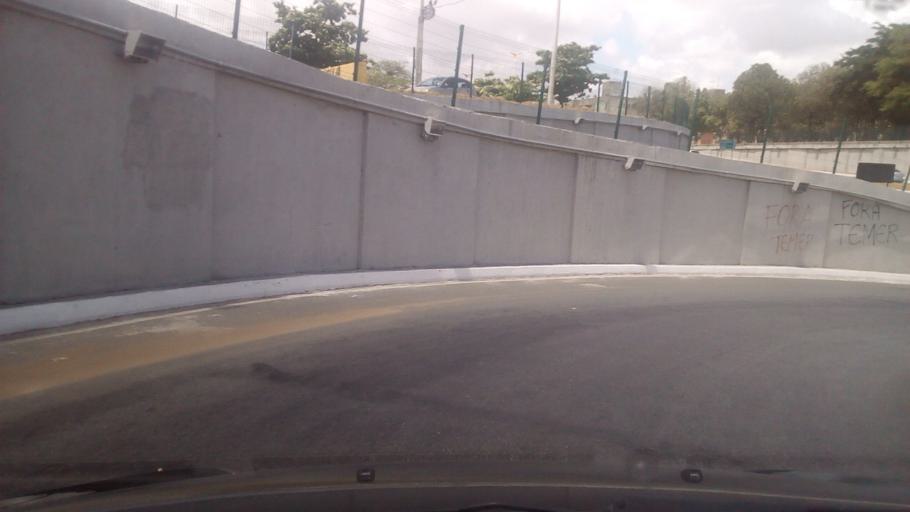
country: BR
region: Paraiba
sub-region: Joao Pessoa
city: Joao Pessoa
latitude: -7.1621
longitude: -34.8387
